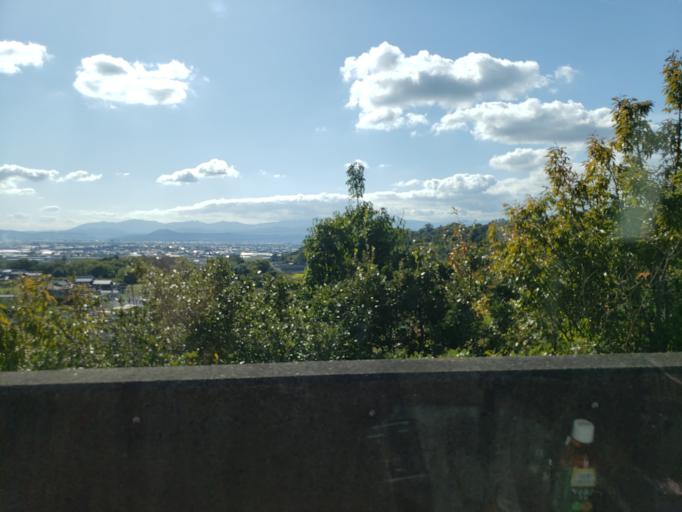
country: JP
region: Tokushima
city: Ishii
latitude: 34.1432
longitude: 134.4290
